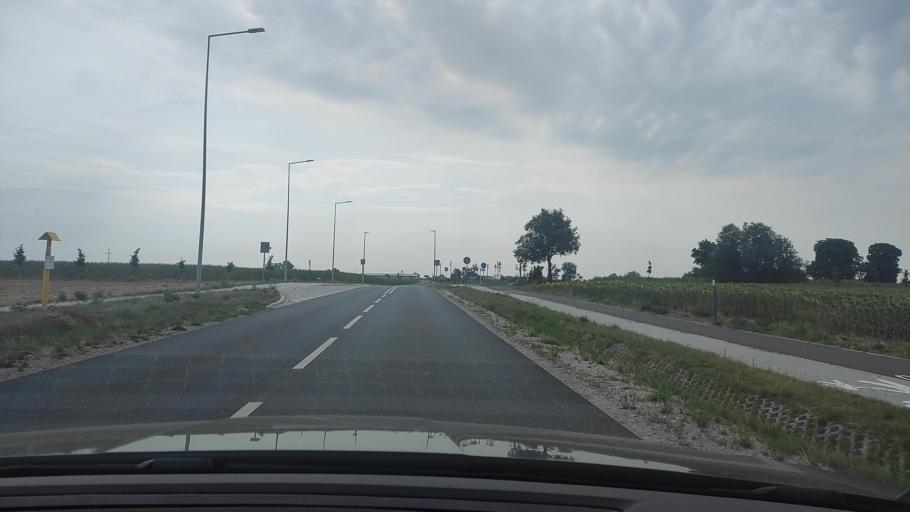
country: PL
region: Greater Poland Voivodeship
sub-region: Powiat poznanski
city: Kornik
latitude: 52.2969
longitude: 17.0969
